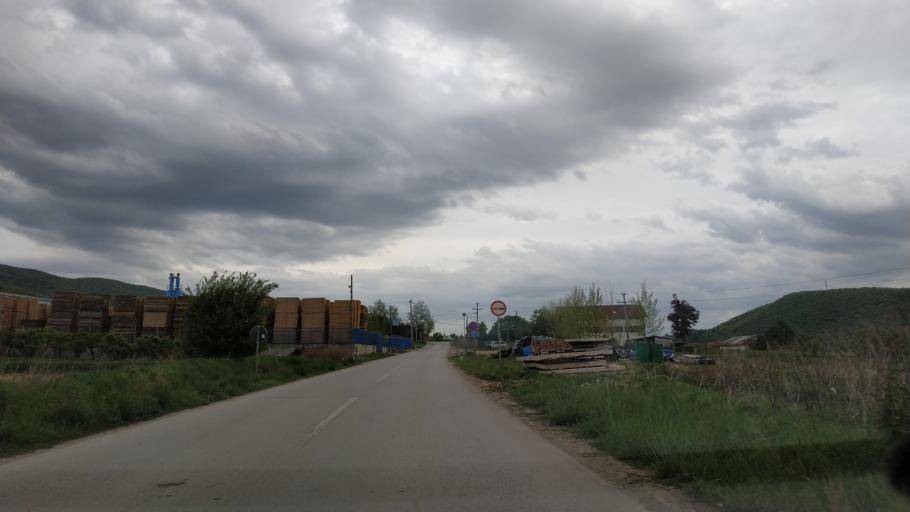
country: RS
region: Central Serbia
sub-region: Nisavski Okrug
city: Aleksinac
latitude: 43.5971
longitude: 21.6893
